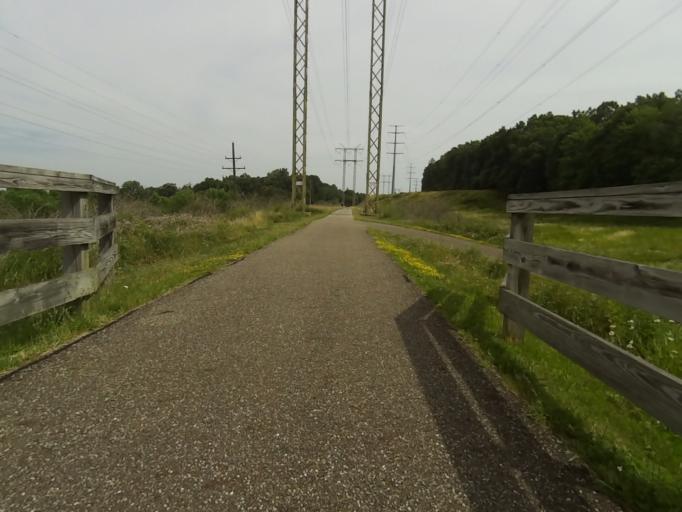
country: US
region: Ohio
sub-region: Cuyahoga County
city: Walton Hills
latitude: 41.3401
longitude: -81.5714
